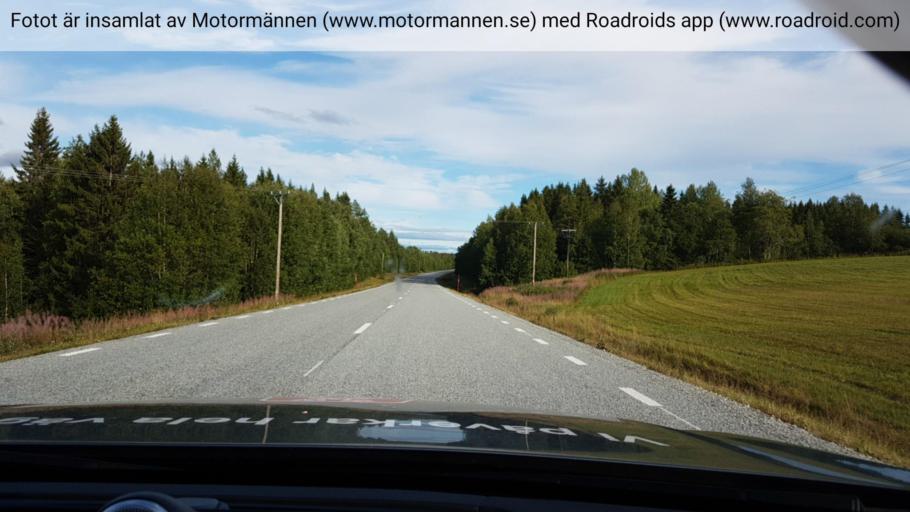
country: SE
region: Jaemtland
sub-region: Stroemsunds Kommun
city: Stroemsund
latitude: 64.2142
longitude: 15.5661
